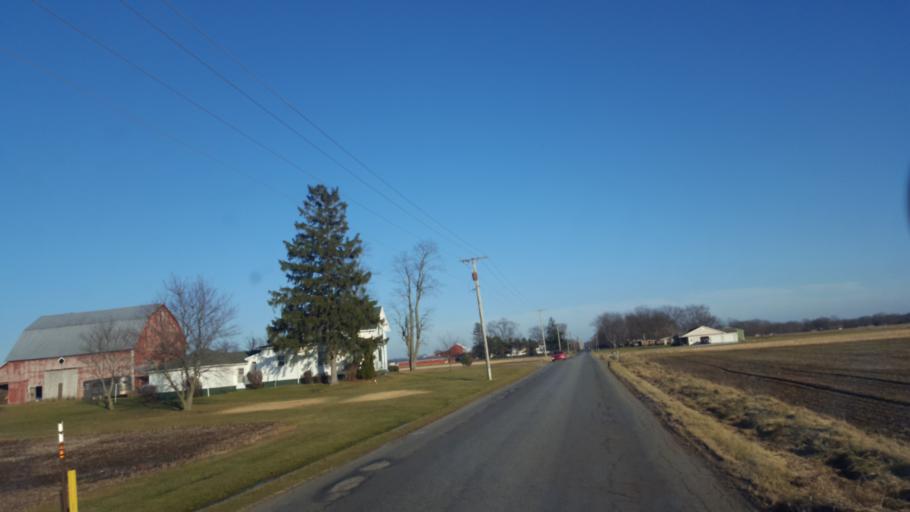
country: US
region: Indiana
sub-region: Elkhart County
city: Nappanee
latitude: 41.4572
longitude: -86.0148
